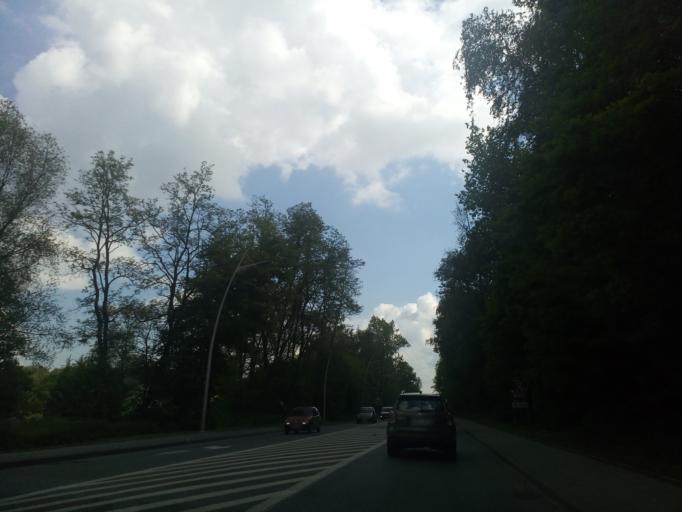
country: PL
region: Lesser Poland Voivodeship
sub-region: Powiat nowosadecki
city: Nowy Sacz
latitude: 49.6455
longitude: 20.6908
